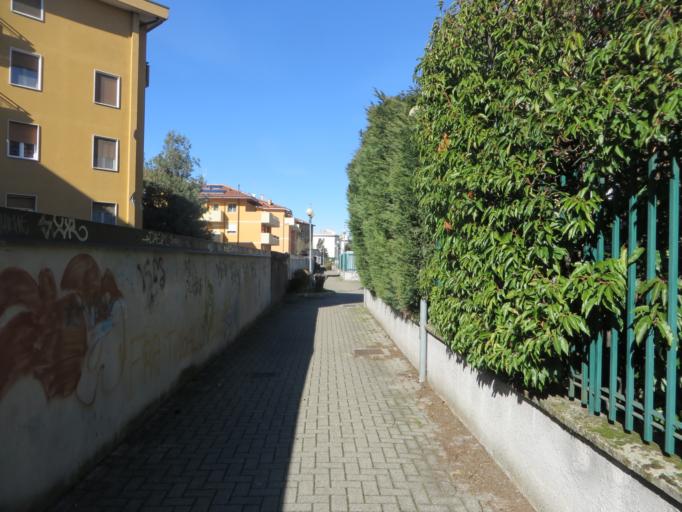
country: IT
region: Lombardy
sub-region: Citta metropolitana di Milano
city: Cornaredo
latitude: 45.4892
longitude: 9.0231
